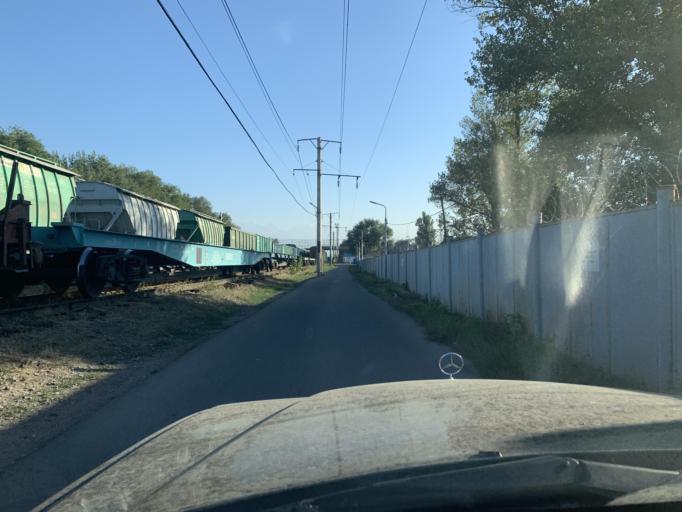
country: KZ
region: Almaty Oblysy
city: Energeticheskiy
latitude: 43.3874
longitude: 76.9984
